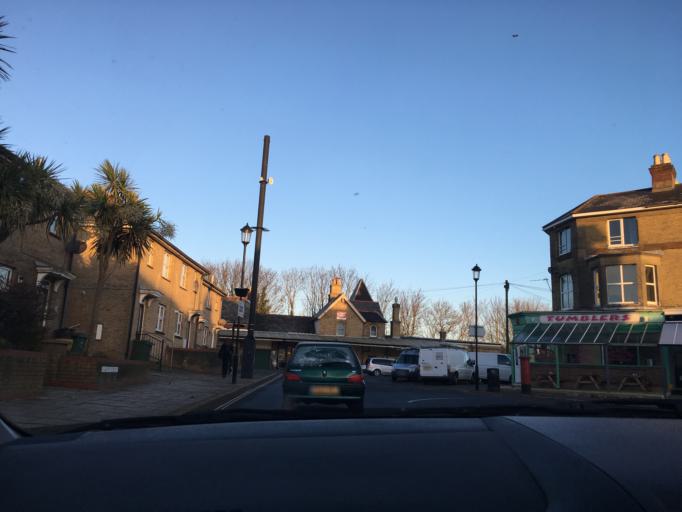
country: GB
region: England
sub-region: Isle of Wight
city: Shanklin
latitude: 50.6333
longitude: -1.1794
